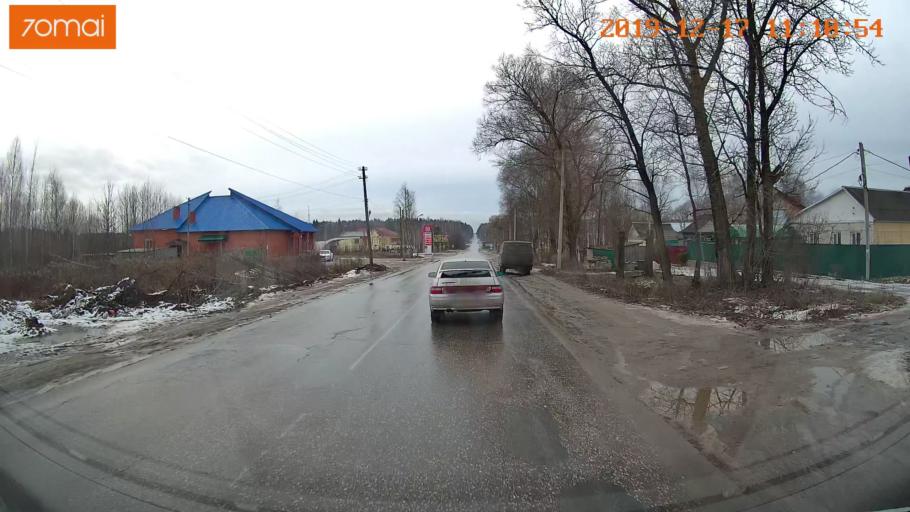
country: RU
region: Vladimir
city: Gus'-Khrustal'nyy
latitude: 55.5897
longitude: 40.6392
